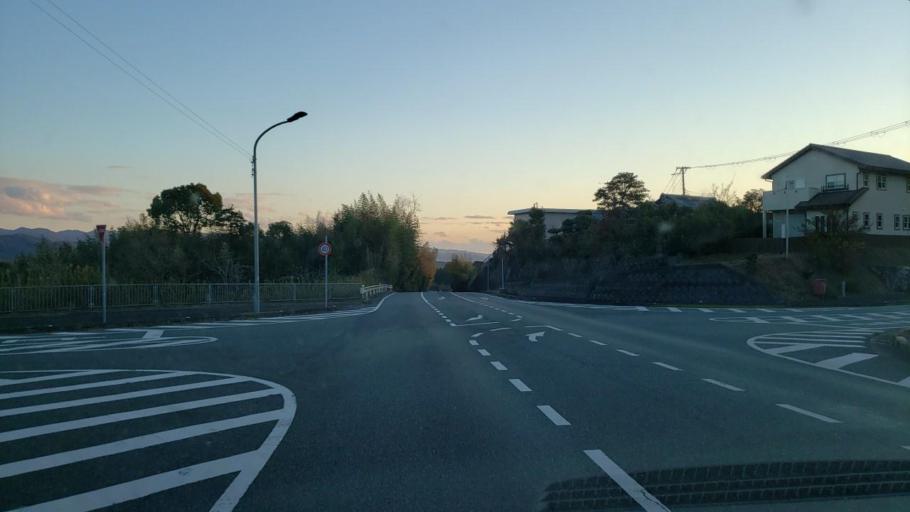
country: JP
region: Hyogo
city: Fukura
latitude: 34.3510
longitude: 134.7834
